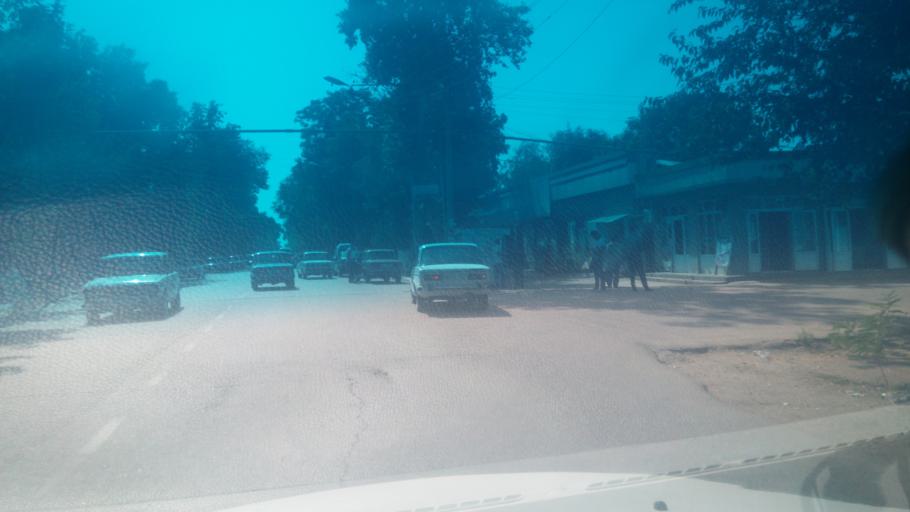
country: UZ
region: Sirdaryo
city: Sirdaryo
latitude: 40.8328
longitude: 68.6653
